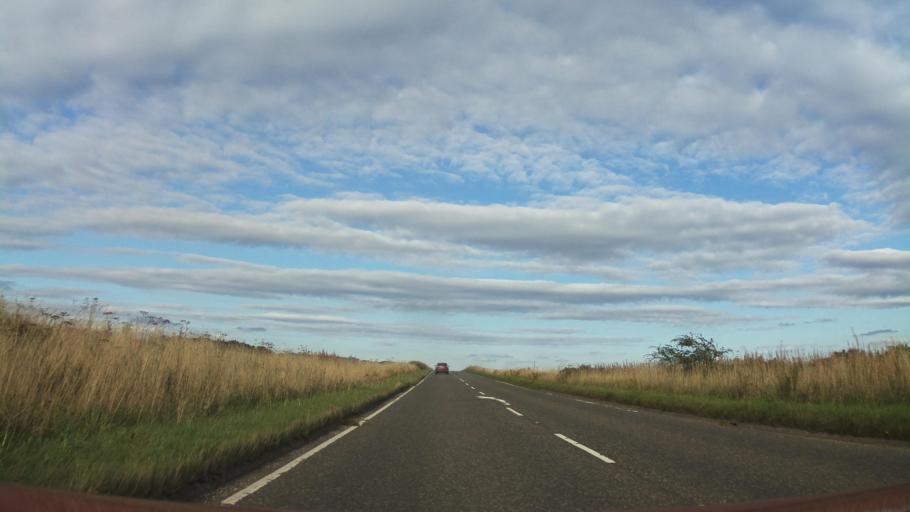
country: GB
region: Scotland
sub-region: Perth and Kinross
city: Milnathort
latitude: 56.2589
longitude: -3.3463
